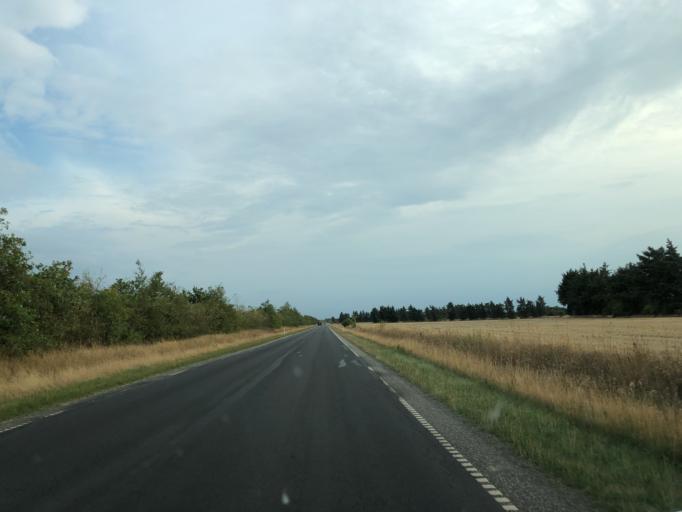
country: DK
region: Central Jutland
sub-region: Struer Kommune
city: Struer
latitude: 56.3927
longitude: 8.4571
